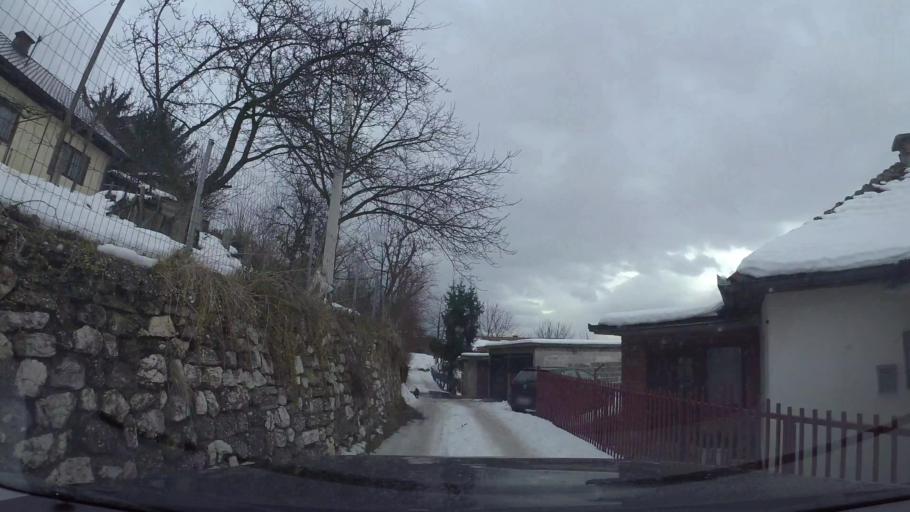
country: BA
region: Federation of Bosnia and Herzegovina
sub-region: Kanton Sarajevo
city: Sarajevo
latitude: 43.8557
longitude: 18.3315
